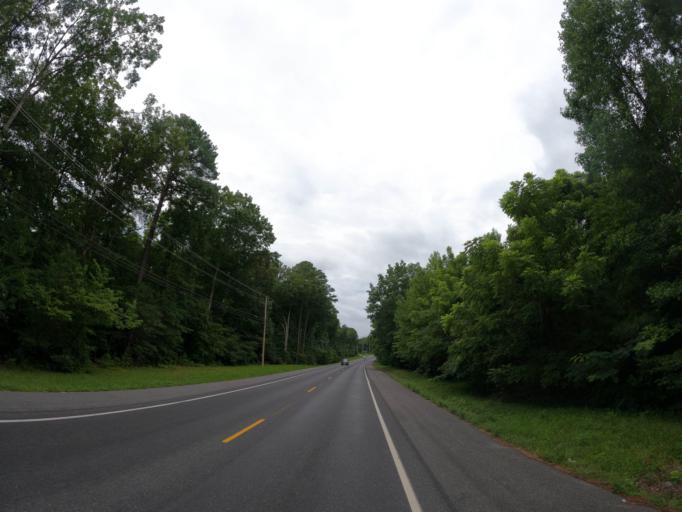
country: US
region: Maryland
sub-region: Saint Mary's County
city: Lexington Park
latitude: 38.1990
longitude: -76.5116
